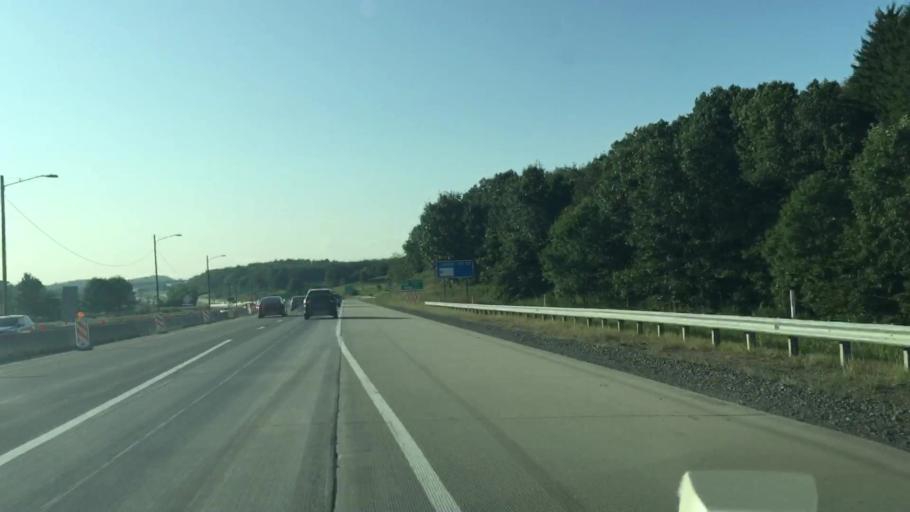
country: US
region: Pennsylvania
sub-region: Allegheny County
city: Imperial
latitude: 40.4732
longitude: -80.2528
